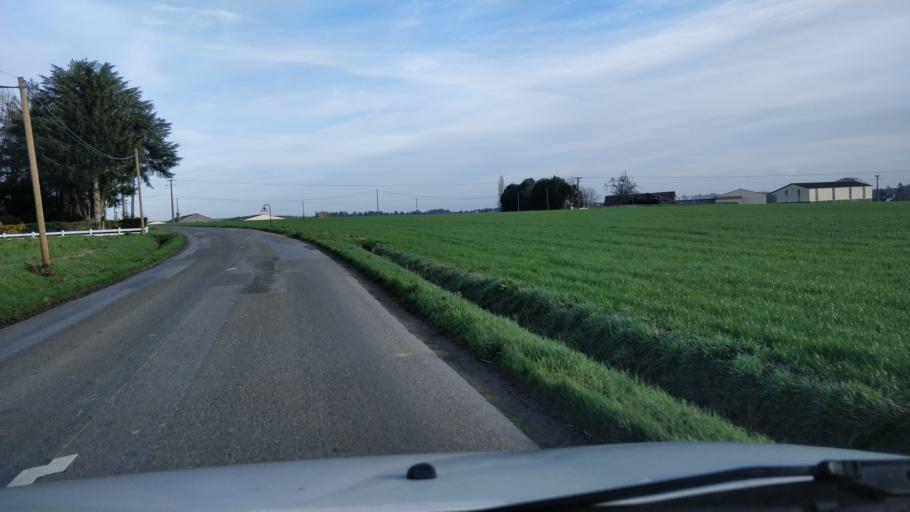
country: FR
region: Brittany
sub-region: Departement d'Ille-et-Vilaine
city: Argentre-du-Plessis
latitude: 48.0482
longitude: -1.1637
